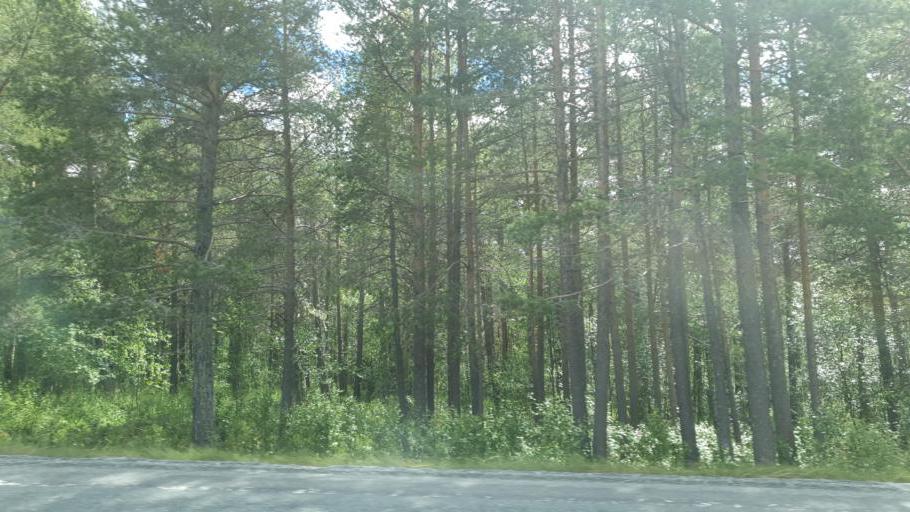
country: NO
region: Sor-Trondelag
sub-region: Oppdal
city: Oppdal
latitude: 62.6486
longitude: 9.8521
